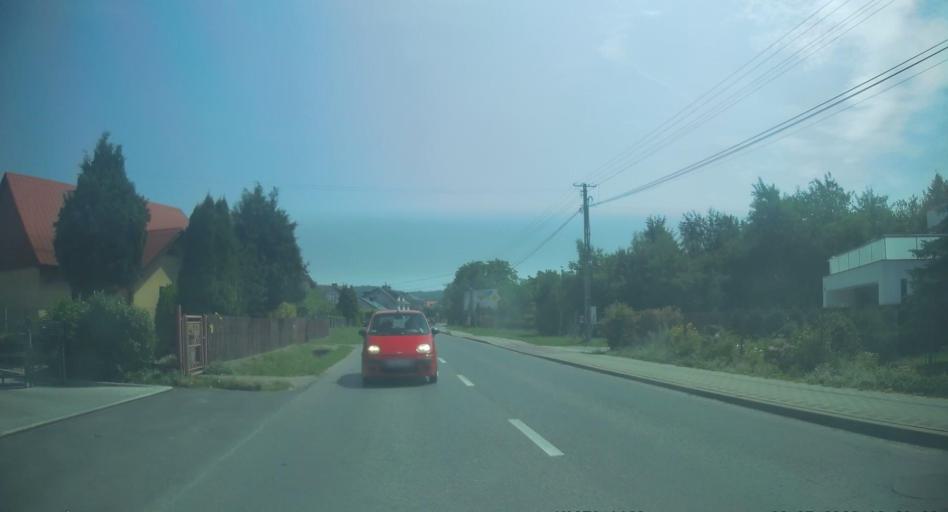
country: PL
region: Subcarpathian Voivodeship
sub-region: Powiat debicki
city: Debica
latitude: 50.0458
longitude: 21.4287
